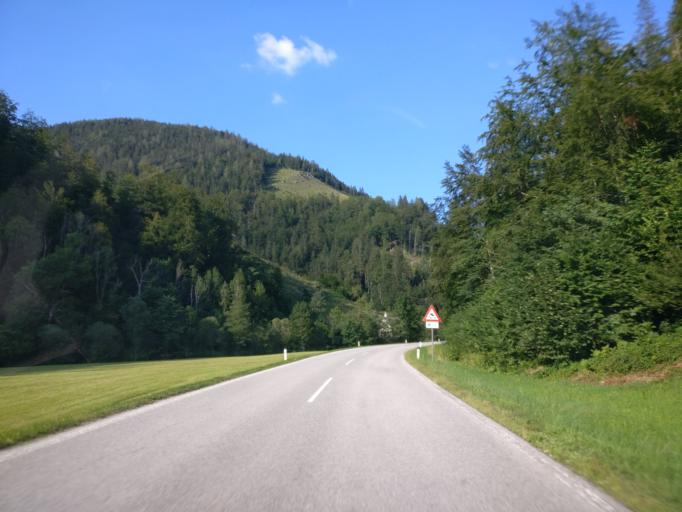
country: AT
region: Lower Austria
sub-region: Politischer Bezirk Scheibbs
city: Gostling an der Ybbs
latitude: 47.7394
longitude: 14.8821
